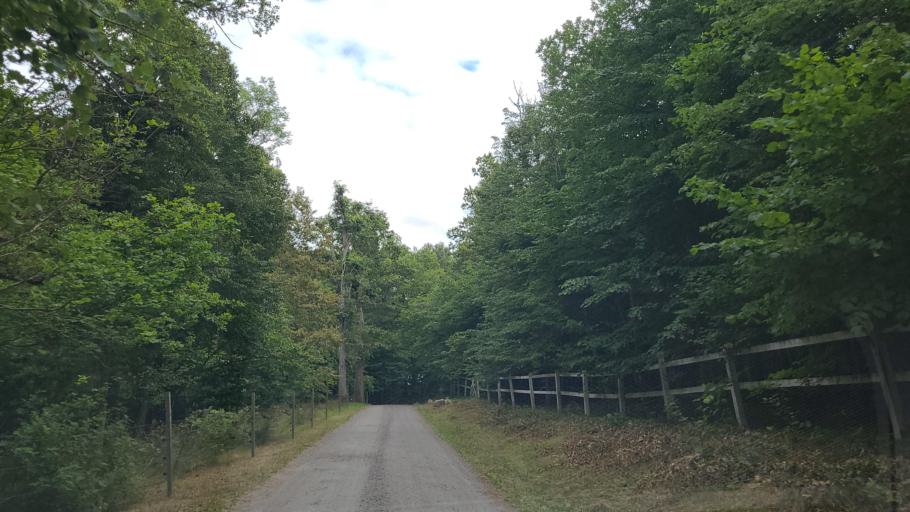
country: SE
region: Stockholm
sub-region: Upplands-Bro Kommun
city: Bro
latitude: 59.4566
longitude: 17.5820
